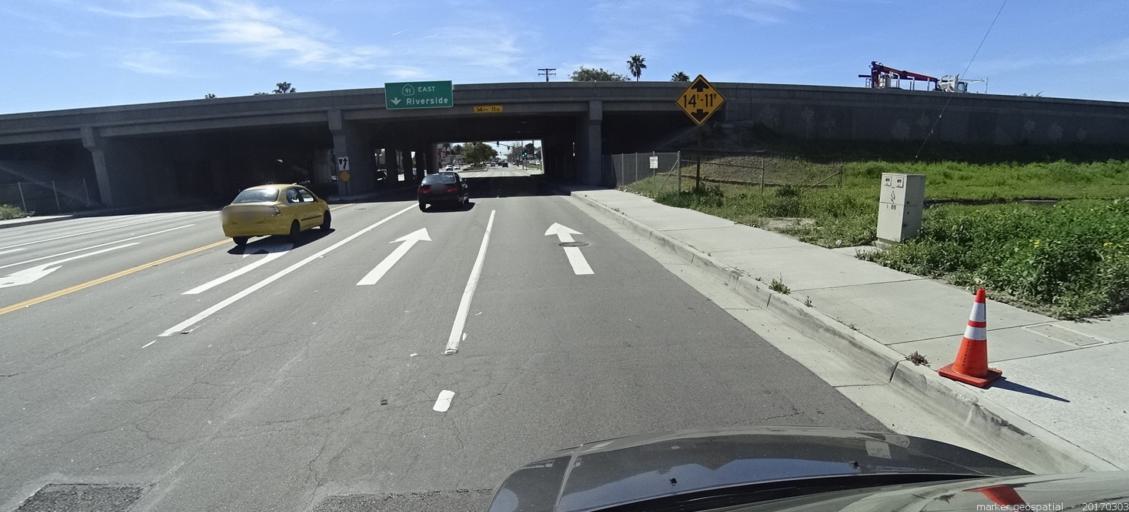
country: US
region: California
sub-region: Orange County
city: Fullerton
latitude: 33.8548
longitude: -117.9419
